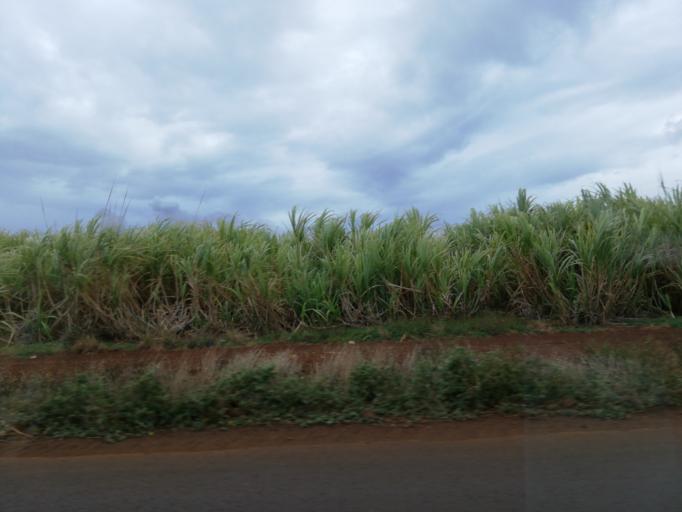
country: MU
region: Black River
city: Petite Riviere
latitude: -20.2102
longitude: 57.4553
